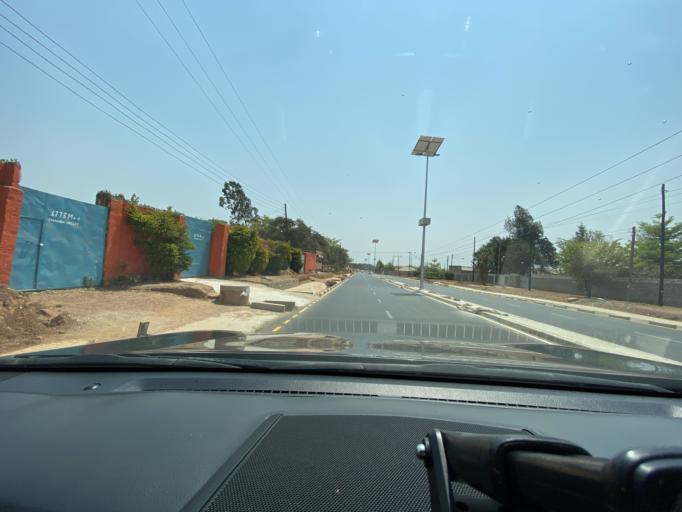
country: ZM
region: Lusaka
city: Lusaka
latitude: -15.3700
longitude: 28.3460
